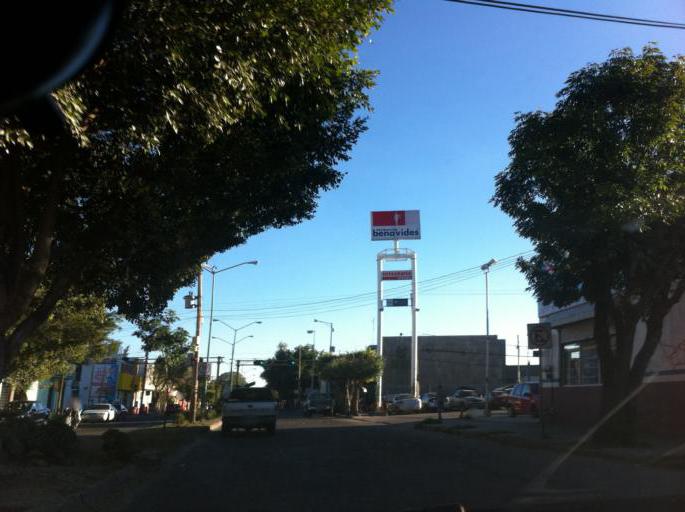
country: MX
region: Guanajuato
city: Leon
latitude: 21.1093
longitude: -101.6873
